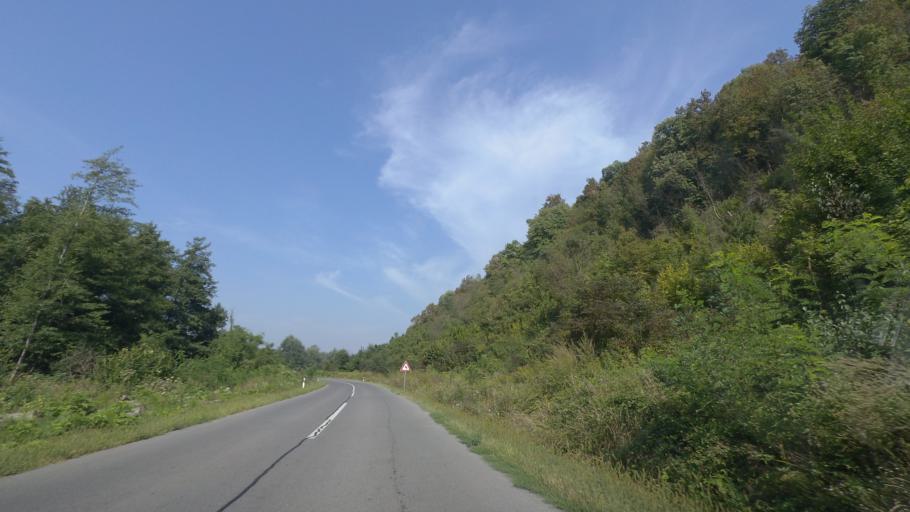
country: BA
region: Republika Srpska
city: Kostajnica
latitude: 45.2216
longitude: 16.6265
